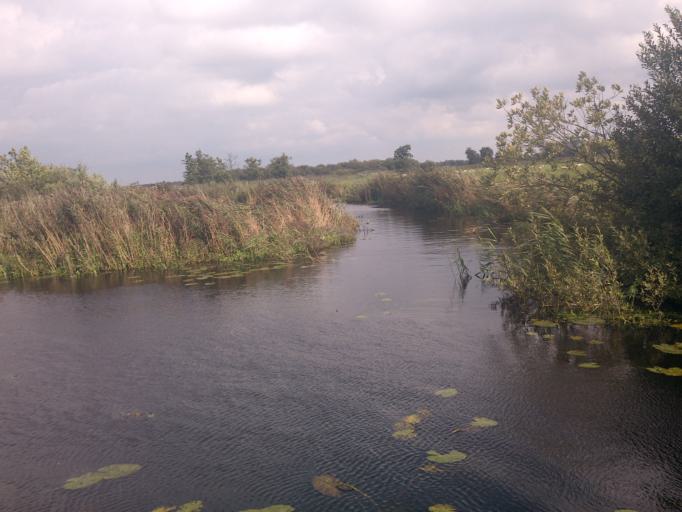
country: NL
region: Friesland
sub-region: Gemeente Smallingerland
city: Oudega
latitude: 53.1064
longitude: 5.9496
